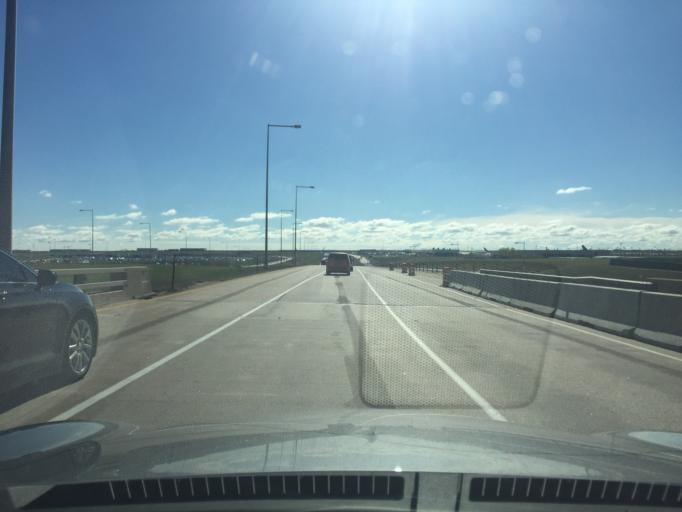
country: US
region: Colorado
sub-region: Adams County
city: Aurora
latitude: 39.8335
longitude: -104.6928
